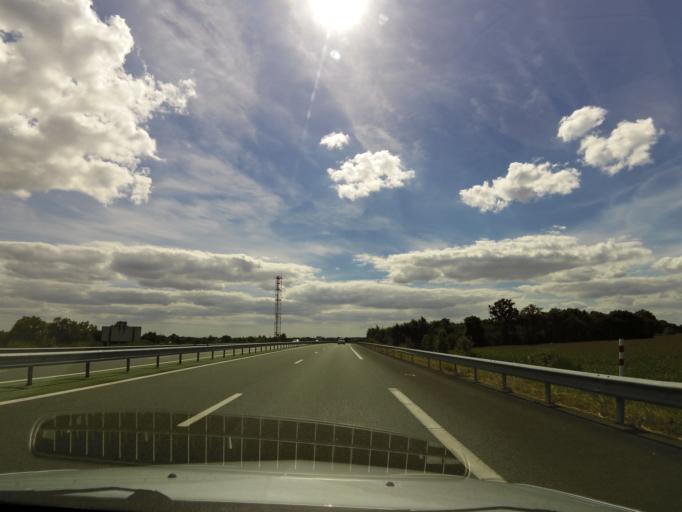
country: FR
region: Pays de la Loire
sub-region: Departement de la Vendee
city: La Ferriere
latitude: 46.6799
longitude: -1.3317
